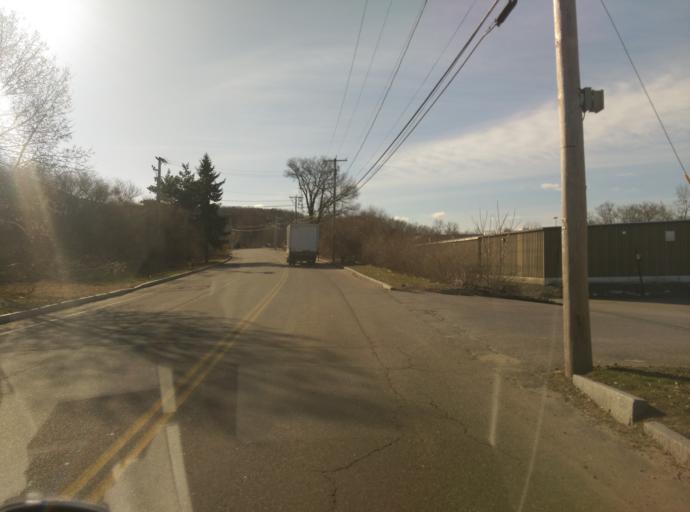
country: US
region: Massachusetts
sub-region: Essex County
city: Haverhill
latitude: 42.7614
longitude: -71.1174
